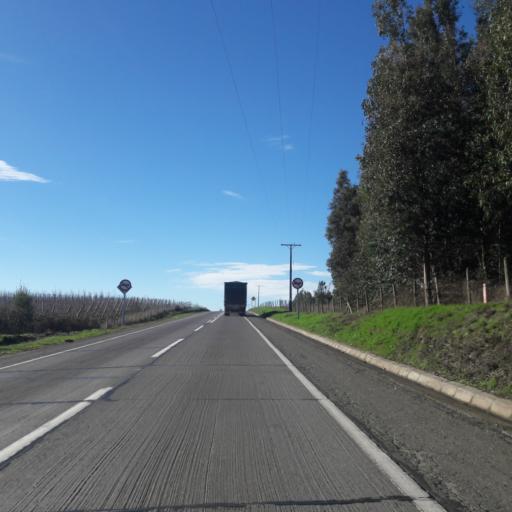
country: CL
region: Araucania
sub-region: Provincia de Malleco
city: Angol
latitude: -37.7429
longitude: -72.6057
